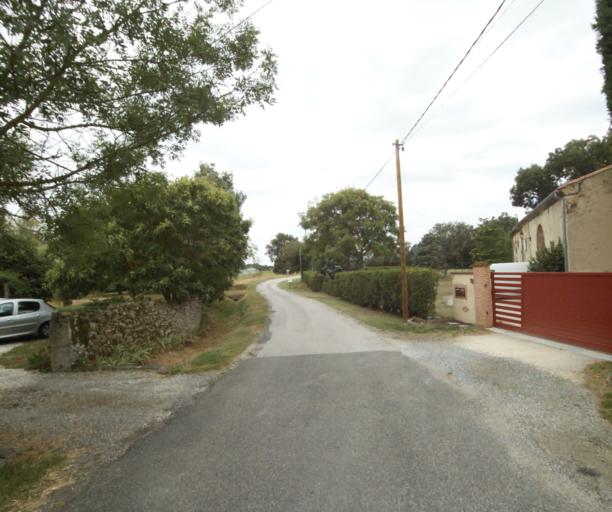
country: FR
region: Midi-Pyrenees
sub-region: Departement de la Haute-Garonne
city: Revel
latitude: 43.4307
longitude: 1.9531
